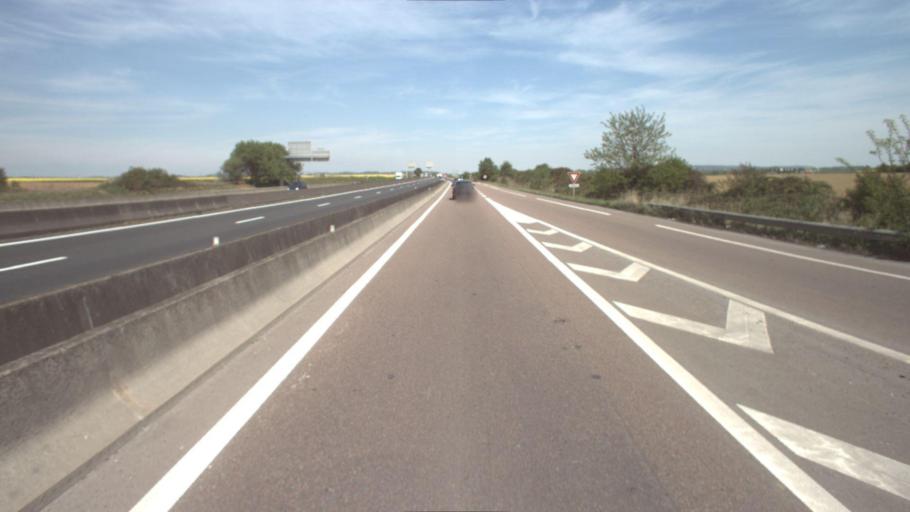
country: FR
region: Ile-de-France
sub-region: Departement de Seine-et-Marne
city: Mitry-Mory
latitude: 49.0028
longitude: 2.6414
